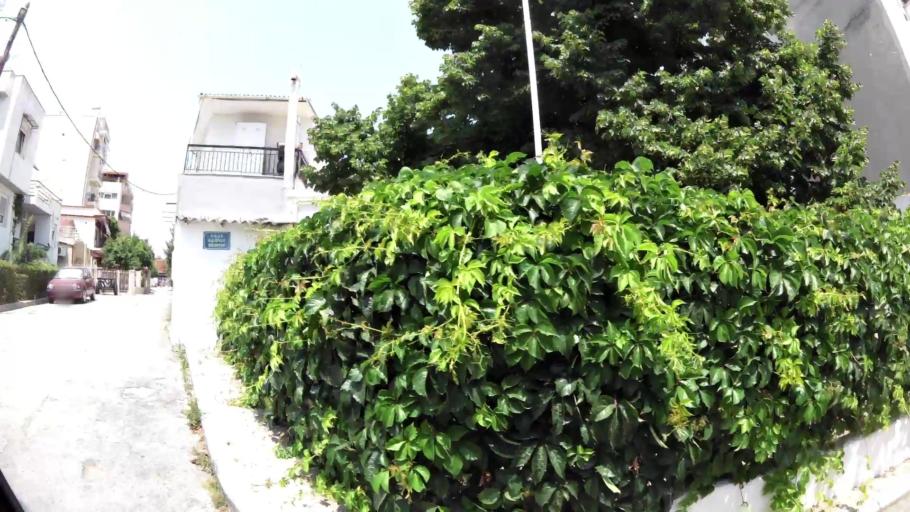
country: GR
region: Central Macedonia
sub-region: Nomos Thessalonikis
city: Evosmos
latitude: 40.6644
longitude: 22.9099
